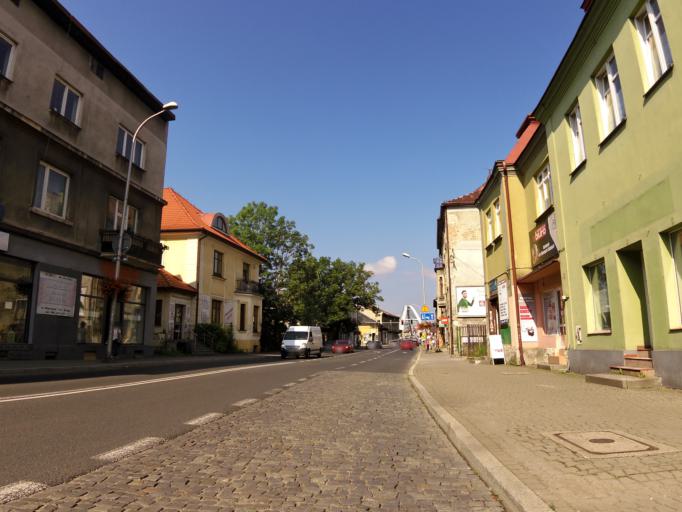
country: PL
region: Silesian Voivodeship
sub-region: Powiat zywiecki
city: Zywiec
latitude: 49.6841
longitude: 19.1908
